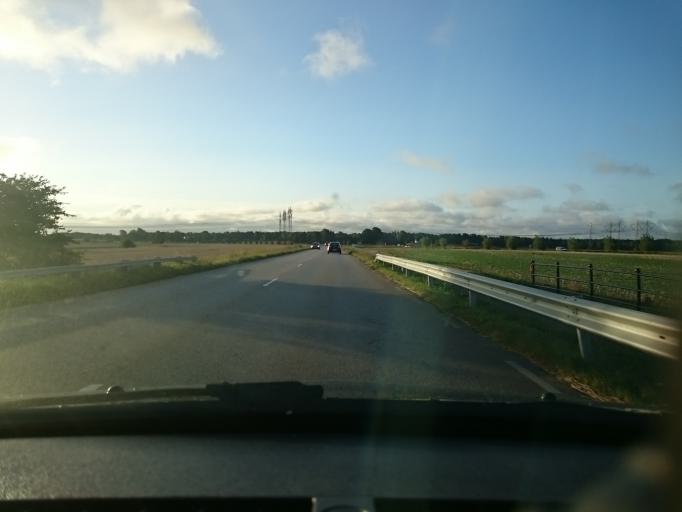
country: SE
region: Skane
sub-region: Kavlinge Kommun
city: Hofterup
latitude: 55.7686
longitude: 12.9701
